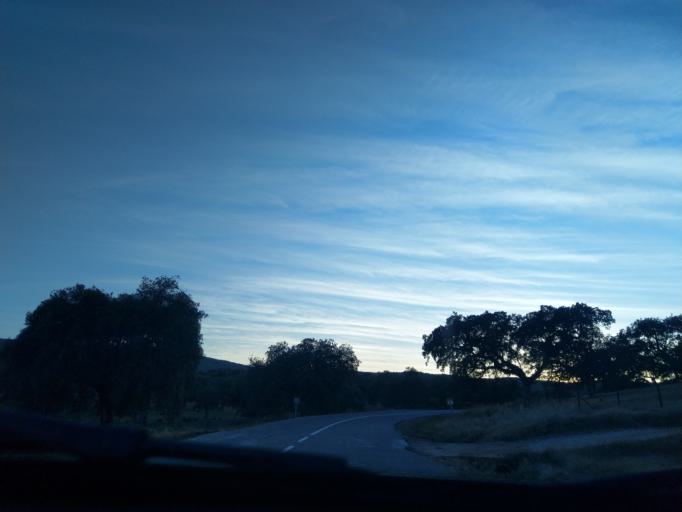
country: ES
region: Extremadura
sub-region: Provincia de Badajoz
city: Reina
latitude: 38.1658
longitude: -5.8871
